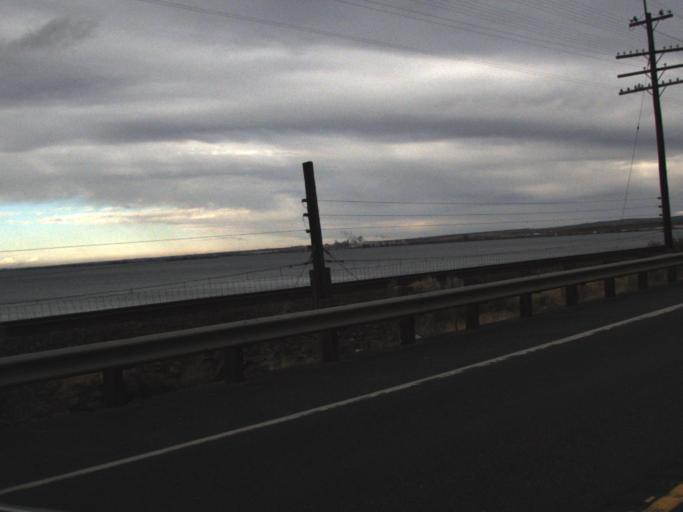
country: US
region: Washington
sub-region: Benton County
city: Finley
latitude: 46.0558
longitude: -118.9305
